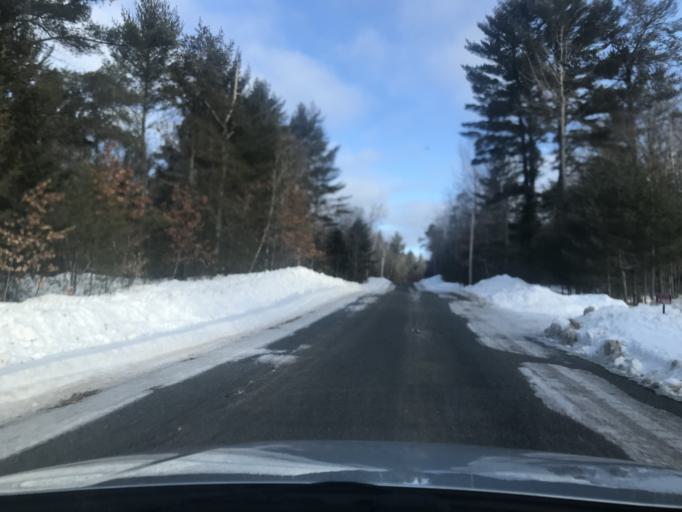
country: US
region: Wisconsin
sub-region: Marinette County
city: Niagara
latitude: 45.6302
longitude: -87.9679
